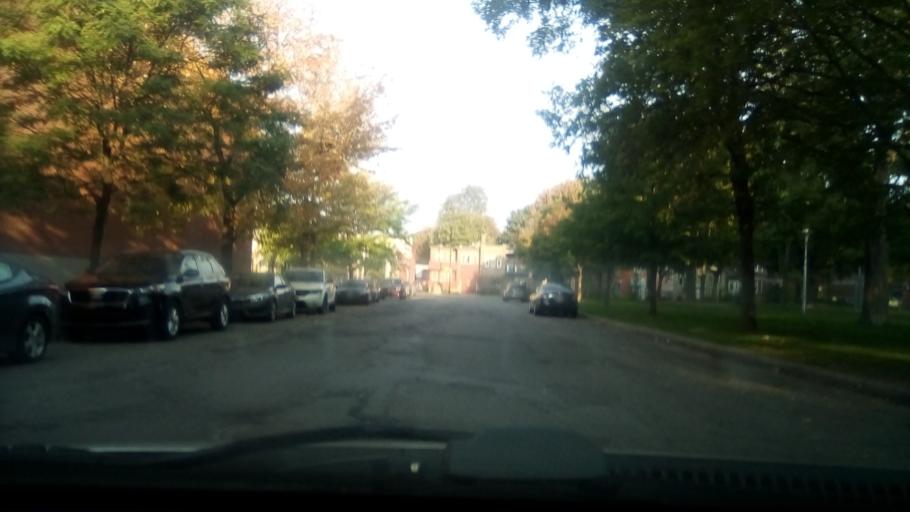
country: CA
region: Quebec
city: Westmount
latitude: 45.4745
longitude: -73.5599
